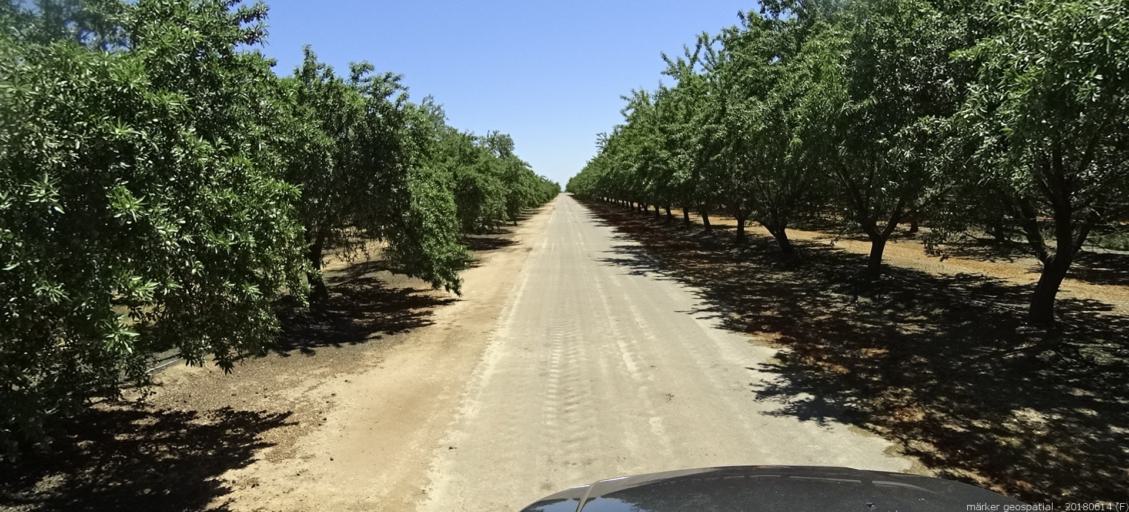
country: US
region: California
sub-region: Madera County
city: Fairmead
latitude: 37.0474
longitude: -120.1874
